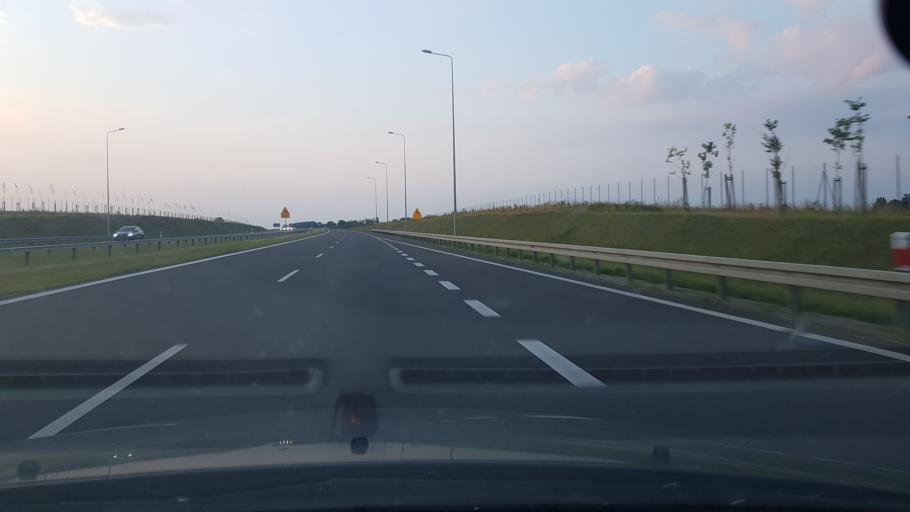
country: PL
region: Warmian-Masurian Voivodeship
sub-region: Powiat nidzicki
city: Nidzica
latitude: 53.2812
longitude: 20.4385
